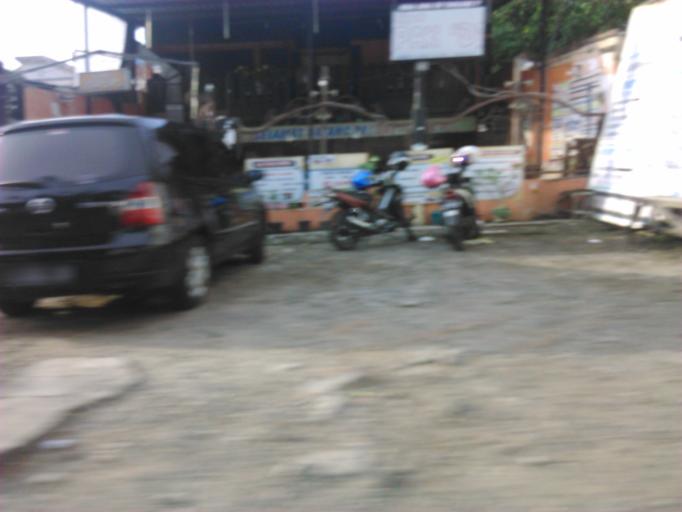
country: ID
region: East Java
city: Semampir
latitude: -7.2894
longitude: 112.7814
